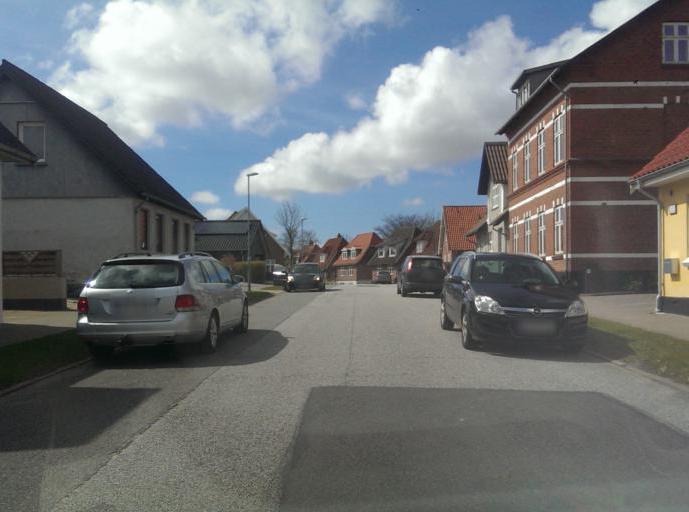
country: DK
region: South Denmark
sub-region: Esbjerg Kommune
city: Esbjerg
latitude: 55.4741
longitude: 8.4850
